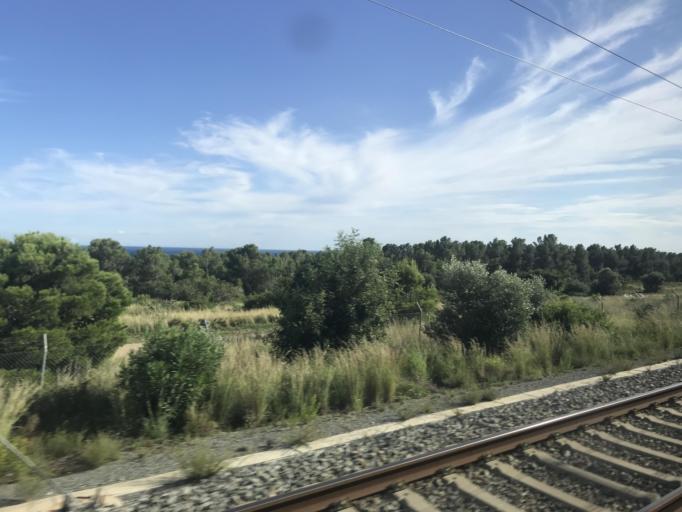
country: ES
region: Catalonia
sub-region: Provincia de Tarragona
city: Colldejou
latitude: 40.9848
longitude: 0.8978
